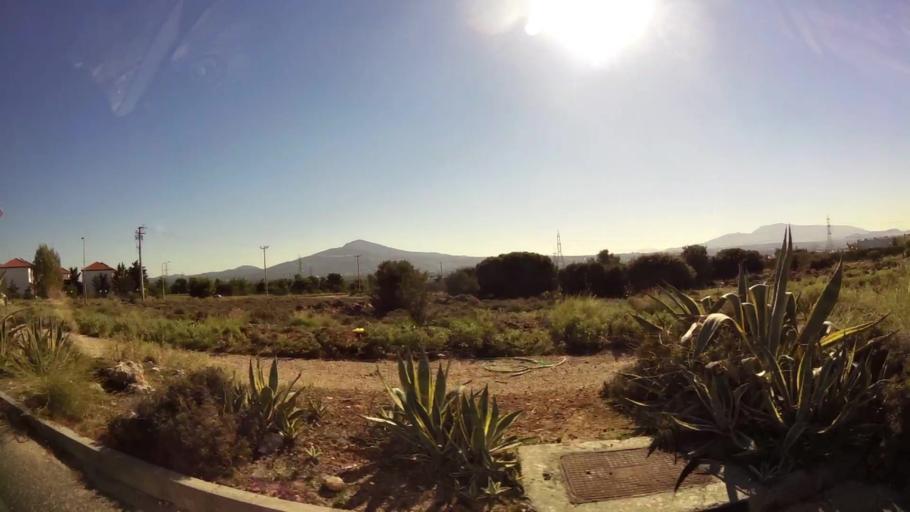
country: GR
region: Attica
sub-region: Nomarchia Anatolikis Attikis
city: Thrakomakedones
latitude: 38.1206
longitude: 23.7640
